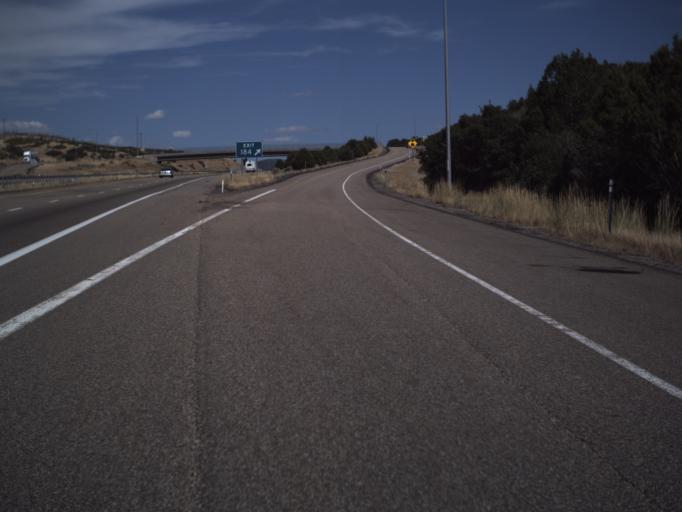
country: US
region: Utah
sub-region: Millard County
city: Fillmore
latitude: 39.2001
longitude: -112.1788
